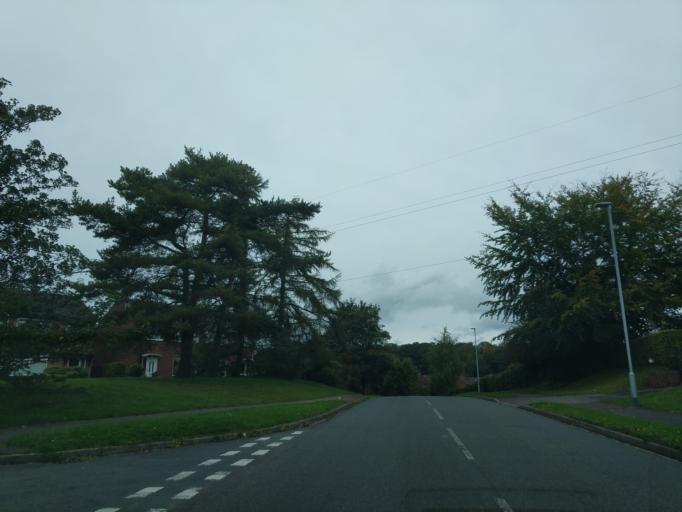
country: GB
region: England
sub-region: Staffordshire
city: Audley
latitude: 53.0036
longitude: -2.3391
